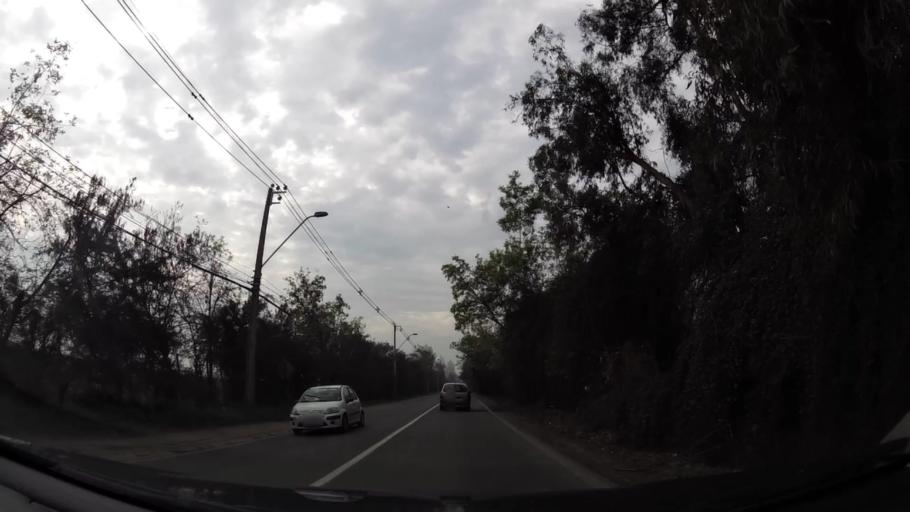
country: CL
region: Santiago Metropolitan
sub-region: Provincia de Chacabuco
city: Chicureo Abajo
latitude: -33.2395
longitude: -70.7504
